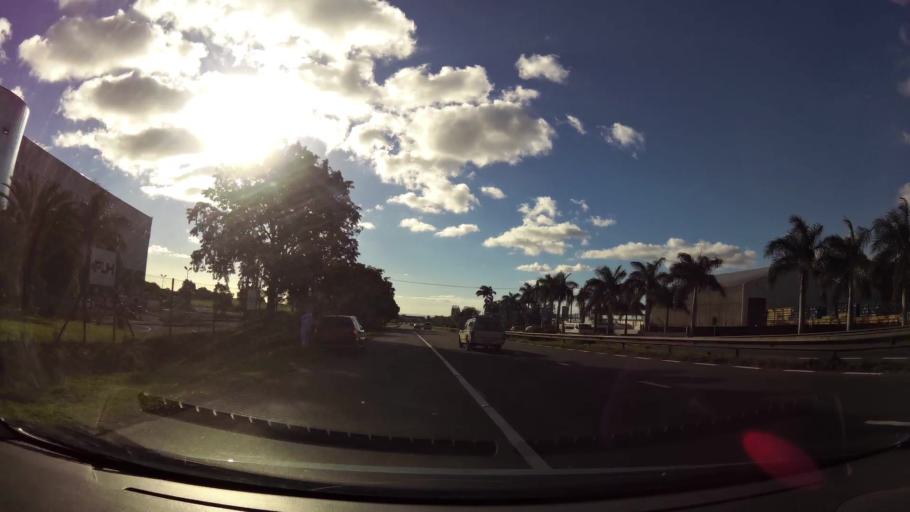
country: MU
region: Plaines Wilhems
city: Quatre Bornes
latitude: -20.2722
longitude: 57.4966
